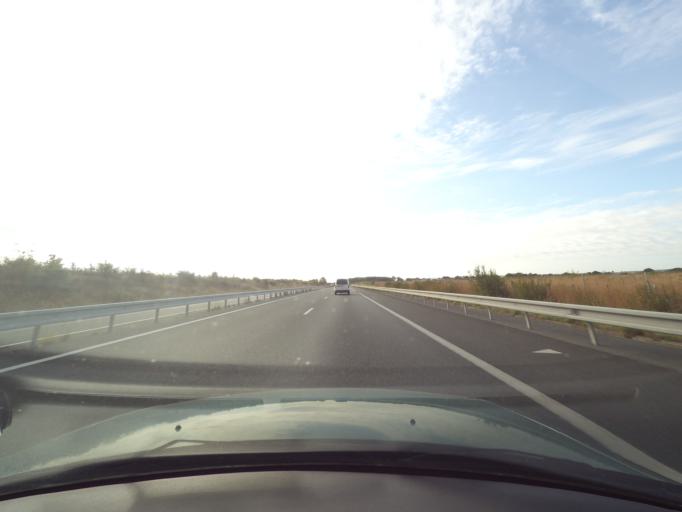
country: FR
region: Poitou-Charentes
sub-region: Departement des Deux-Sevres
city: Saint-Pierre-des-Echaubrognes
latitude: 46.9278
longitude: -0.7188
